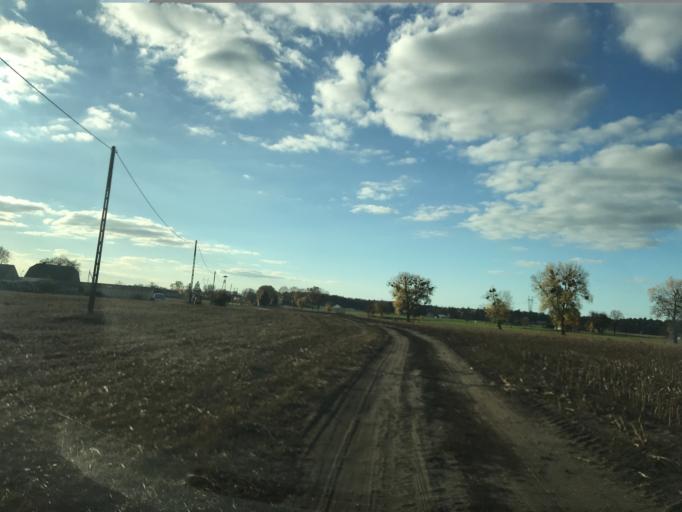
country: PL
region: Warmian-Masurian Voivodeship
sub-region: Powiat dzialdowski
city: Lidzbark
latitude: 53.3689
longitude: 19.8230
